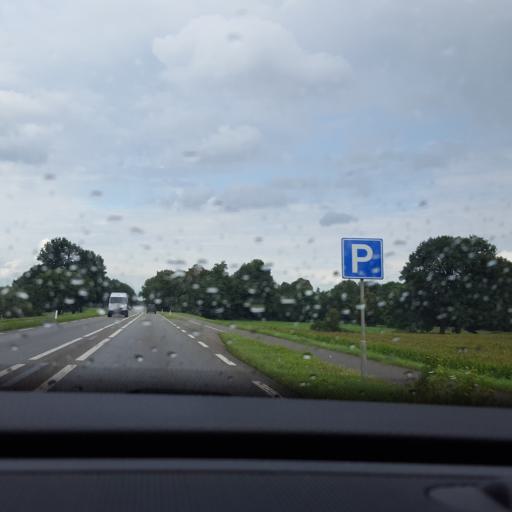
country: NL
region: Gelderland
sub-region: Gemeente Doesburg
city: Doesburg
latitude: 51.9941
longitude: 6.1066
